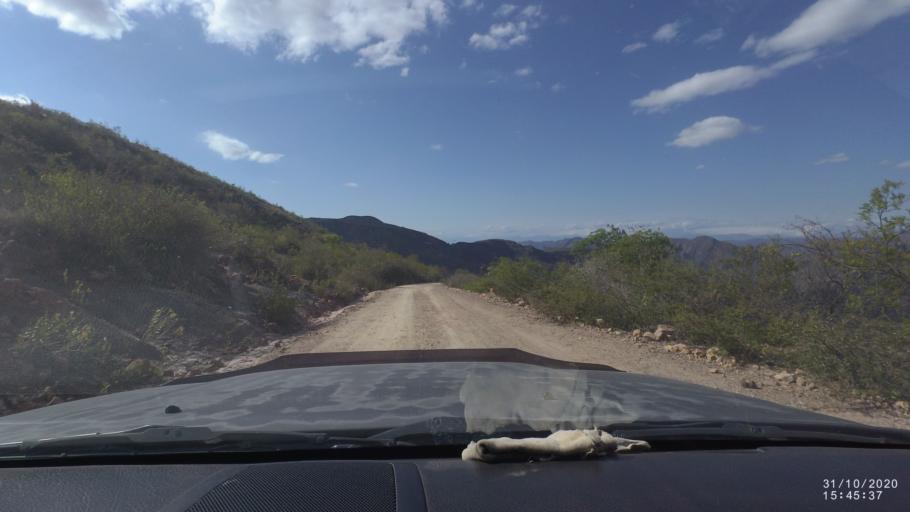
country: BO
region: Chuquisaca
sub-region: Provincia Zudanez
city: Mojocoya
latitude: -18.3182
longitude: -64.7166
